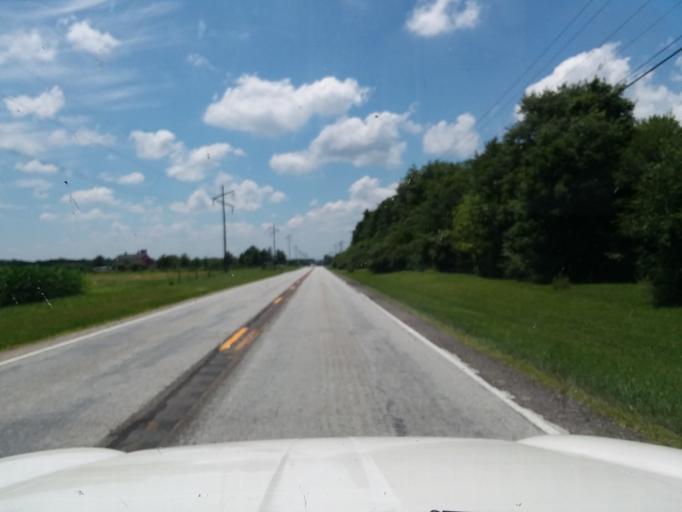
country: US
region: Indiana
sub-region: Johnson County
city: Trafalgar
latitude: 39.3929
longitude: -86.2126
